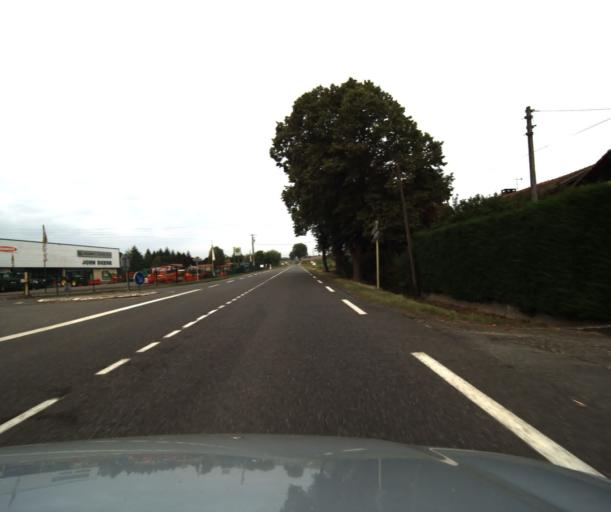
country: FR
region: Midi-Pyrenees
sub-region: Departement du Gers
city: Mielan
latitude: 43.4250
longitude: 0.2850
